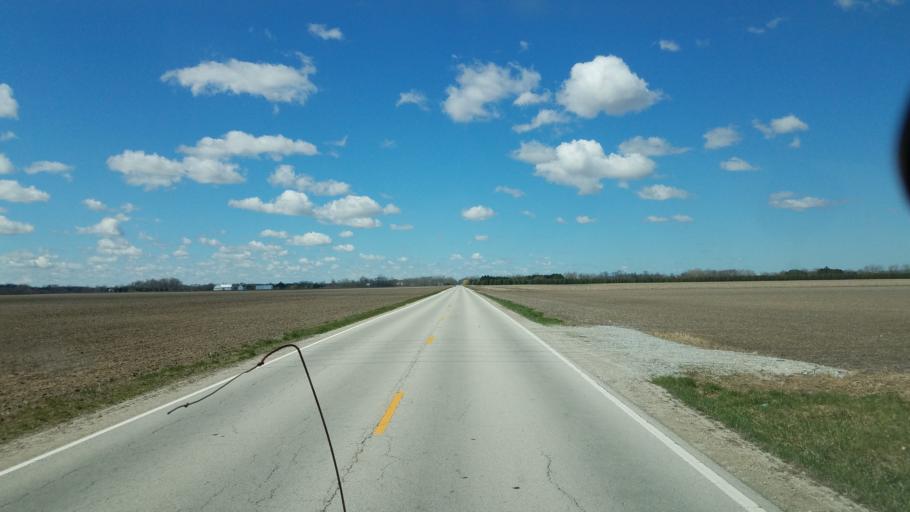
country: US
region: Ohio
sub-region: Sandusky County
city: Ballville
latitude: 41.2917
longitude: -83.1398
